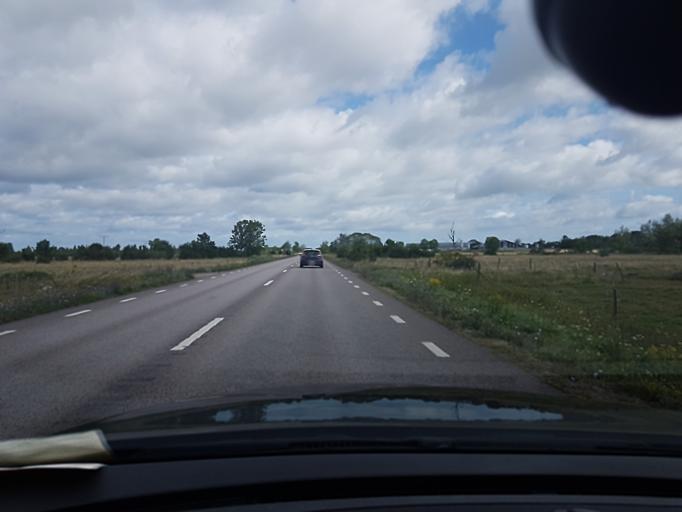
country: SE
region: Kalmar
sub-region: Borgholms Kommun
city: Borgholm
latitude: 56.9448
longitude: 16.7778
